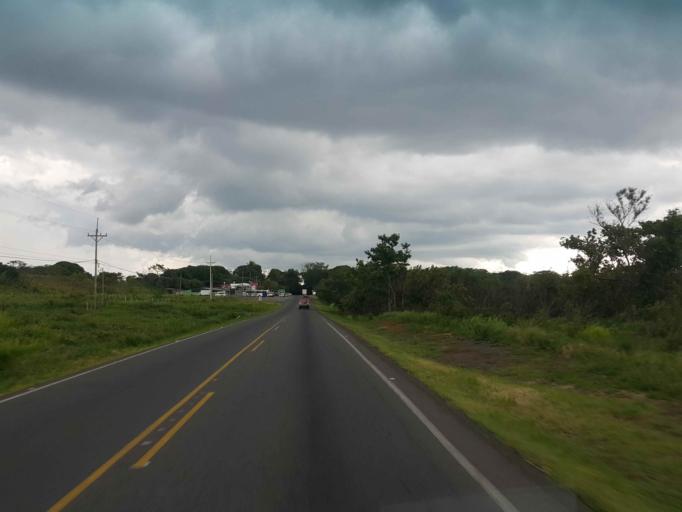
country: CR
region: Puntarenas
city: Miramar
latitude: 10.0973
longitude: -84.8022
